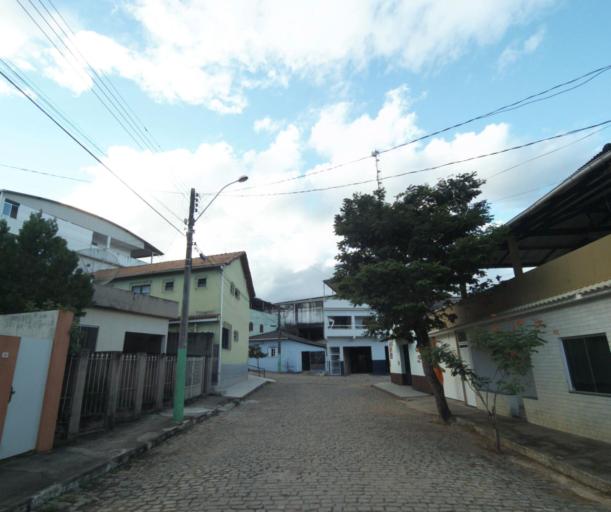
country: BR
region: Espirito Santo
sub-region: Guacui
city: Guacui
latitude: -20.6208
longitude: -41.6848
